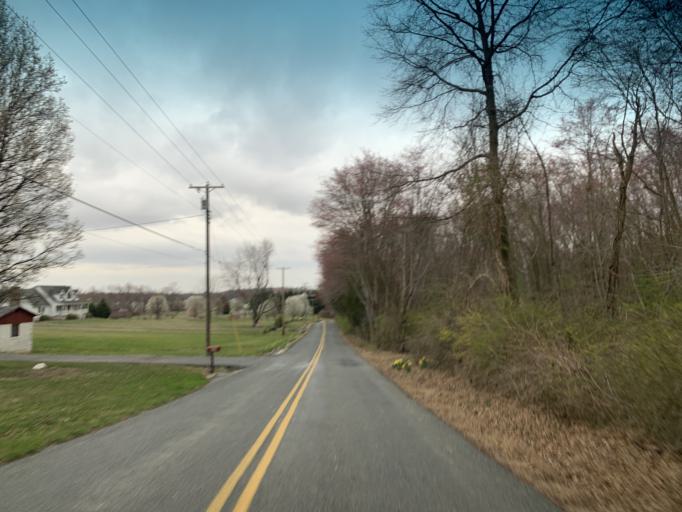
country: US
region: Maryland
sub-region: Harford County
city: Aberdeen
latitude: 39.5484
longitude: -76.1945
